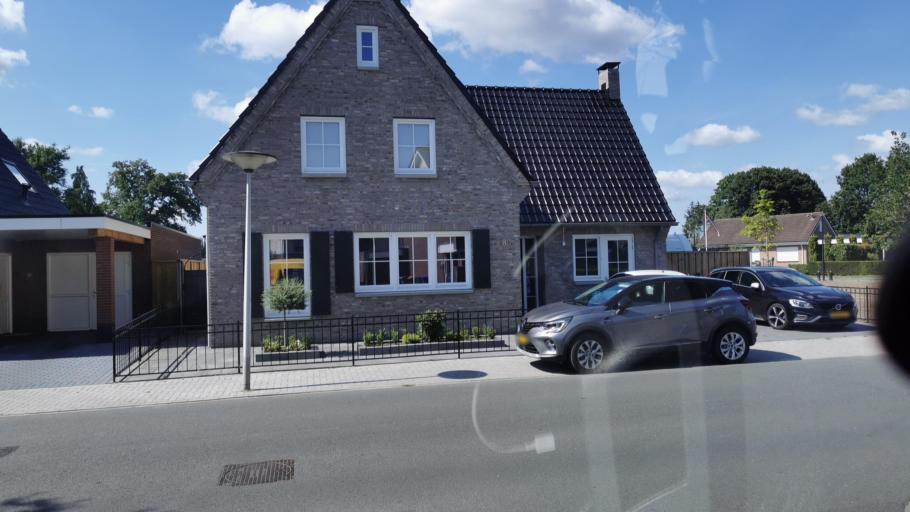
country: DE
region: North Rhine-Westphalia
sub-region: Regierungsbezirk Munster
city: Gronau
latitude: 52.2063
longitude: 6.9631
